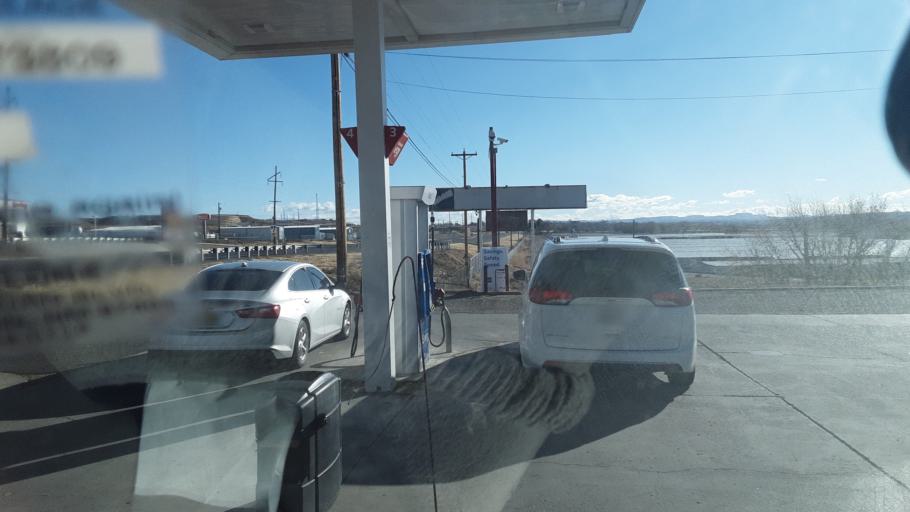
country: US
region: New Mexico
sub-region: San Juan County
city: Lee Acres
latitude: 36.7037
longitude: -108.1056
